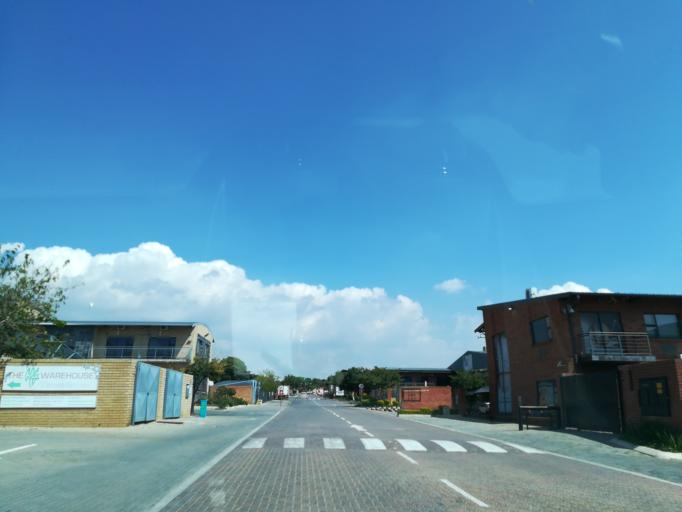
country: ZA
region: Gauteng
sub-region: City of Johannesburg Metropolitan Municipality
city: Diepsloot
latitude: -26.0345
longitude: 27.9599
